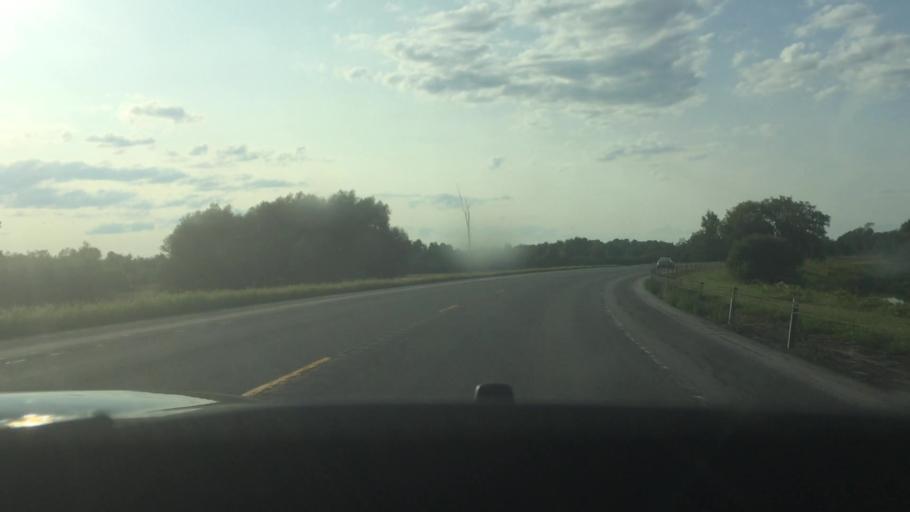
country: US
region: New York
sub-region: St. Lawrence County
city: Canton
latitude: 44.6079
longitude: -75.2106
